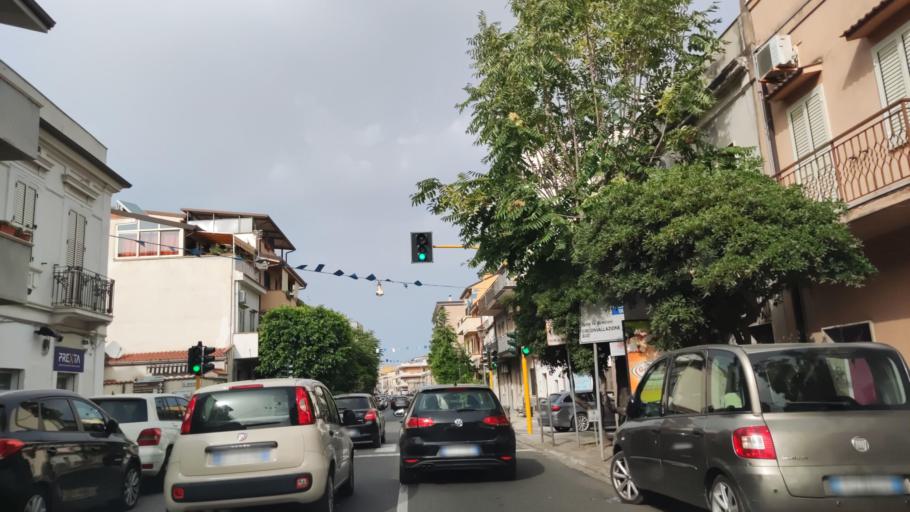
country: IT
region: Calabria
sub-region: Provincia di Reggio Calabria
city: Siderno
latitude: 38.2635
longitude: 16.2918
